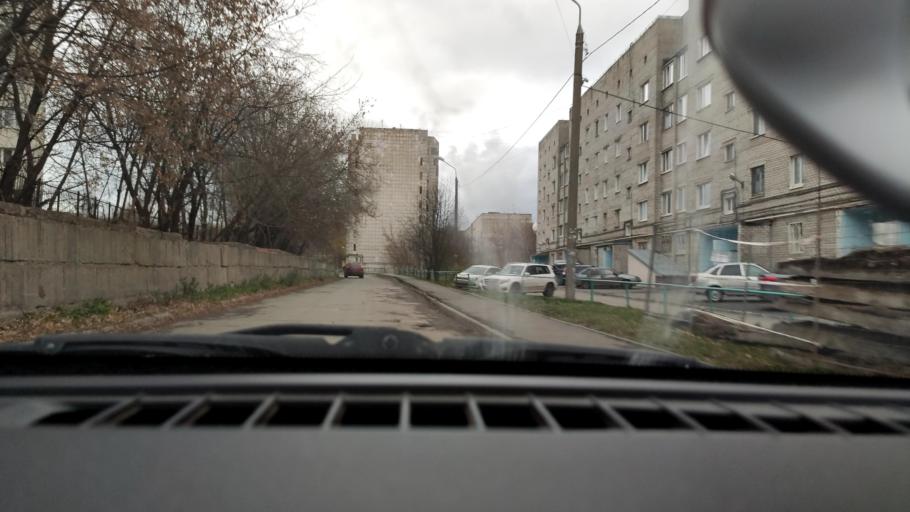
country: RU
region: Perm
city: Perm
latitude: 57.9956
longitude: 56.2724
